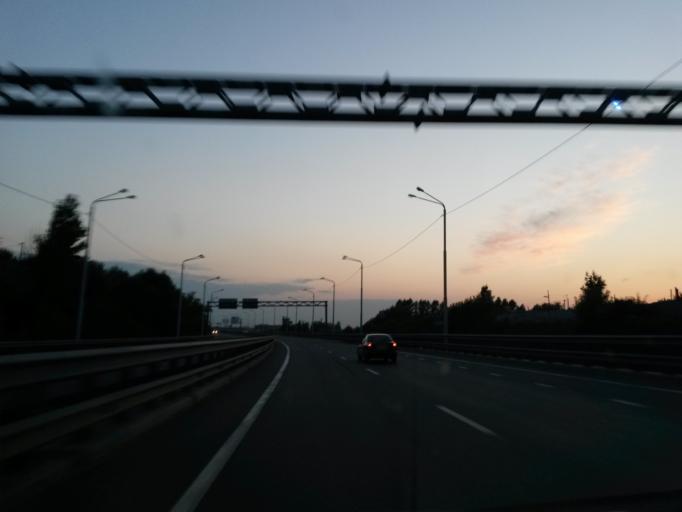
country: RU
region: Jaroslavl
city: Yaroslavl
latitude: 57.6685
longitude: 39.8334
